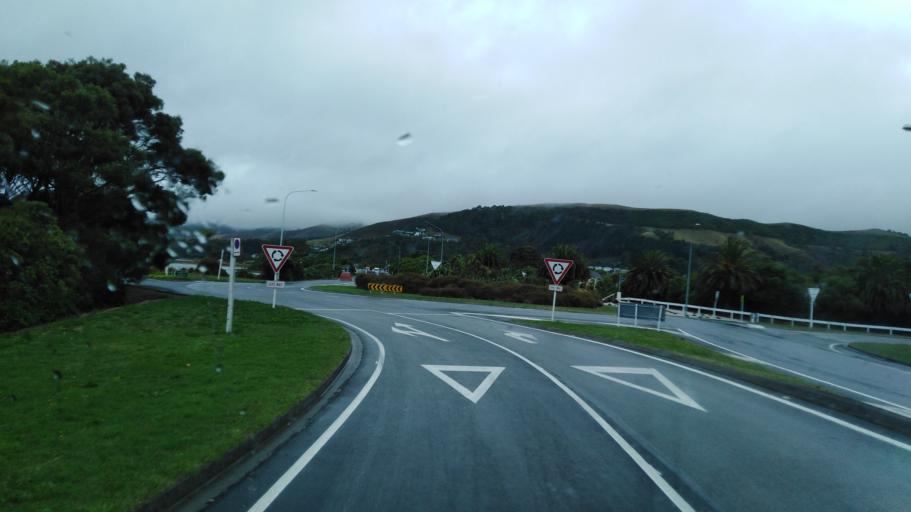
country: NZ
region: Nelson
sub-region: Nelson City
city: Nelson
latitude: -41.2651
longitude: 173.2834
